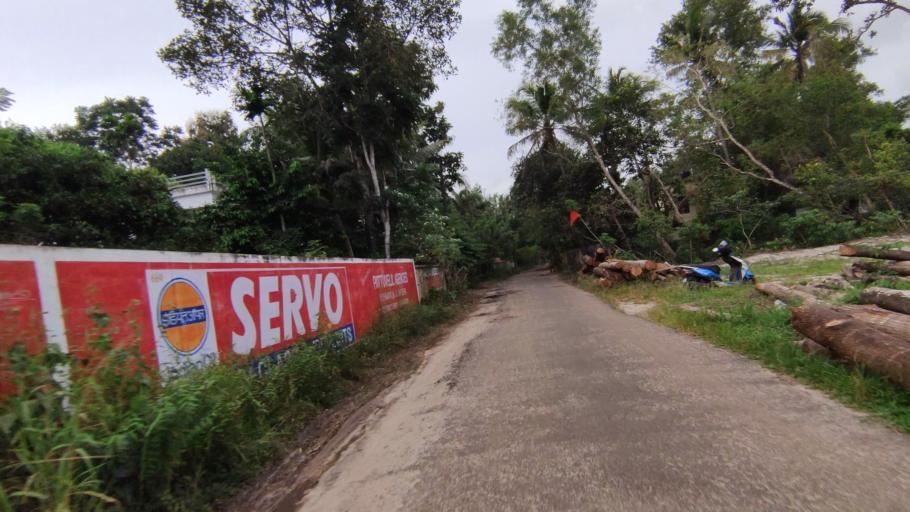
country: IN
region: Kerala
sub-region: Alappuzha
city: Shertallai
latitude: 9.6223
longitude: 76.3557
